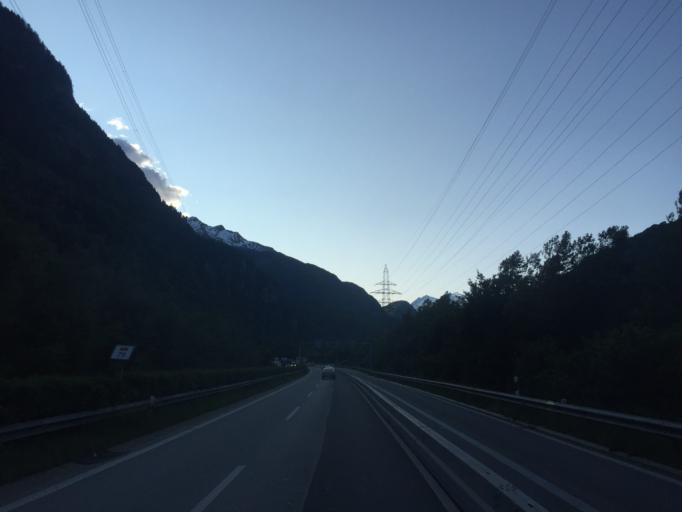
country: CH
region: Ticino
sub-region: Leventina District
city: Bodio
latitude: 46.3878
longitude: 8.8884
